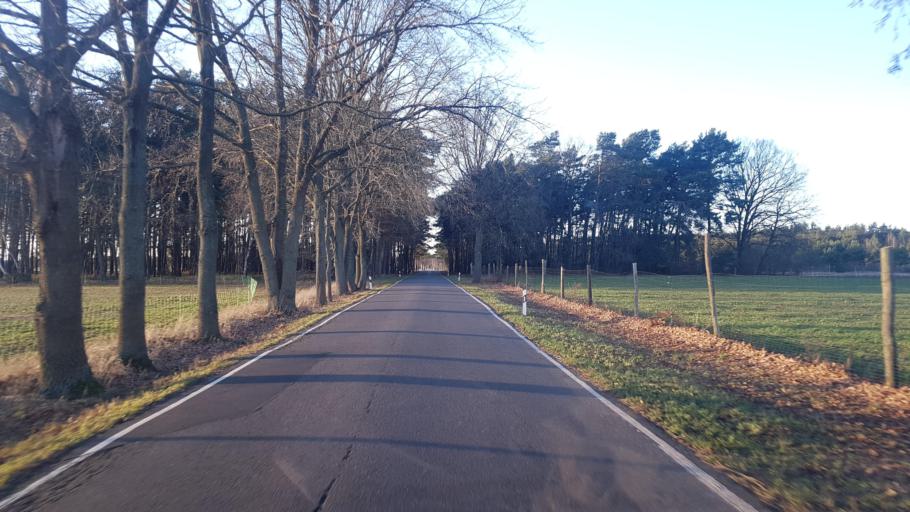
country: DE
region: Brandenburg
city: Drachhausen
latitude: 51.8722
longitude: 14.3318
